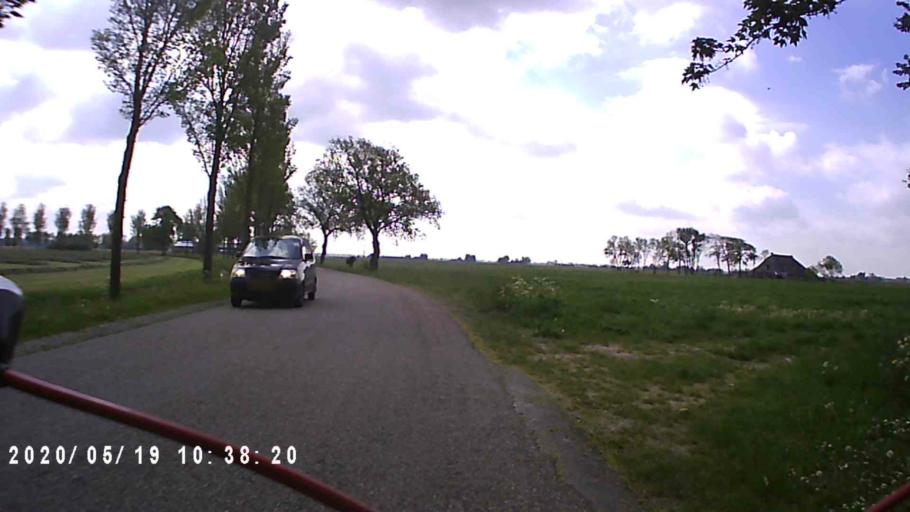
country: NL
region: Friesland
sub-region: Gemeente Kollumerland en Nieuwkruisland
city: Kollum
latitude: 53.2721
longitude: 6.1881
